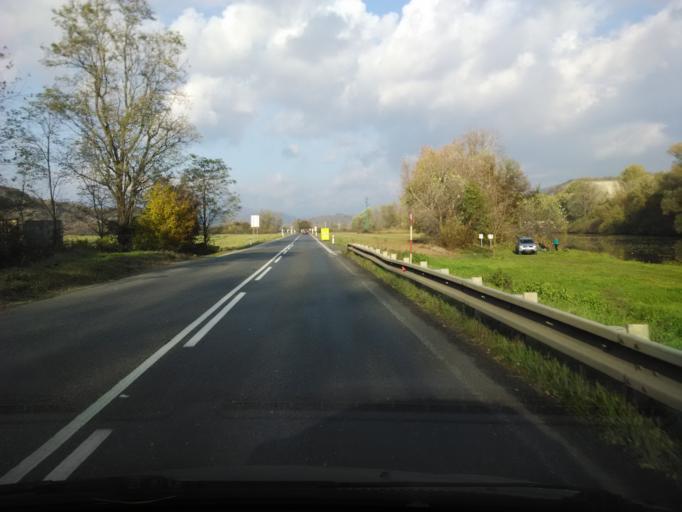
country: SK
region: Nitriansky
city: Tlmace
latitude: 48.2961
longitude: 18.5291
